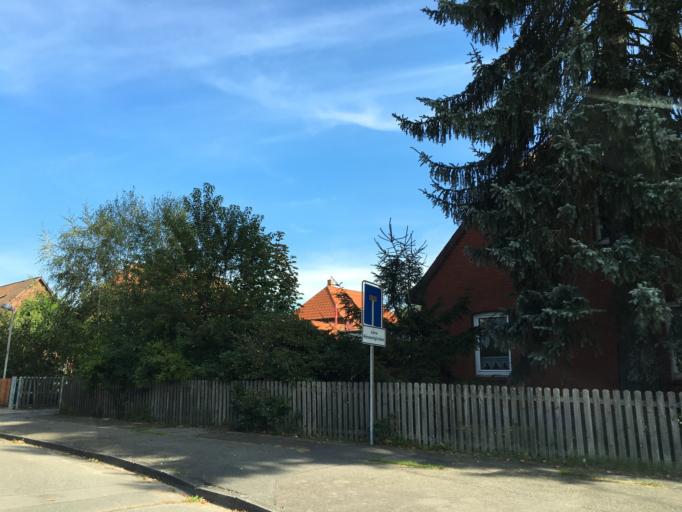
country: DE
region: Lower Saxony
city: Adendorf
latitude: 53.2760
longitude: 10.4743
